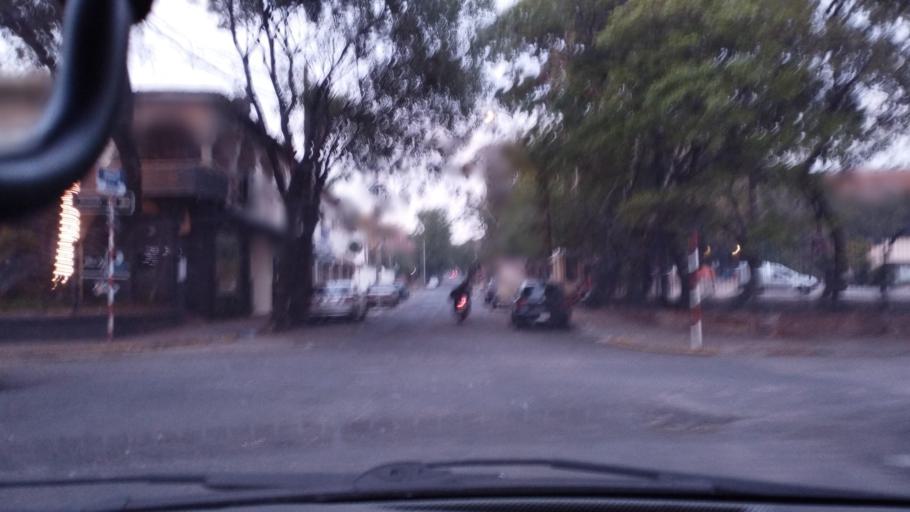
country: PY
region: Asuncion
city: Asuncion
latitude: -25.2952
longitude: -57.5794
